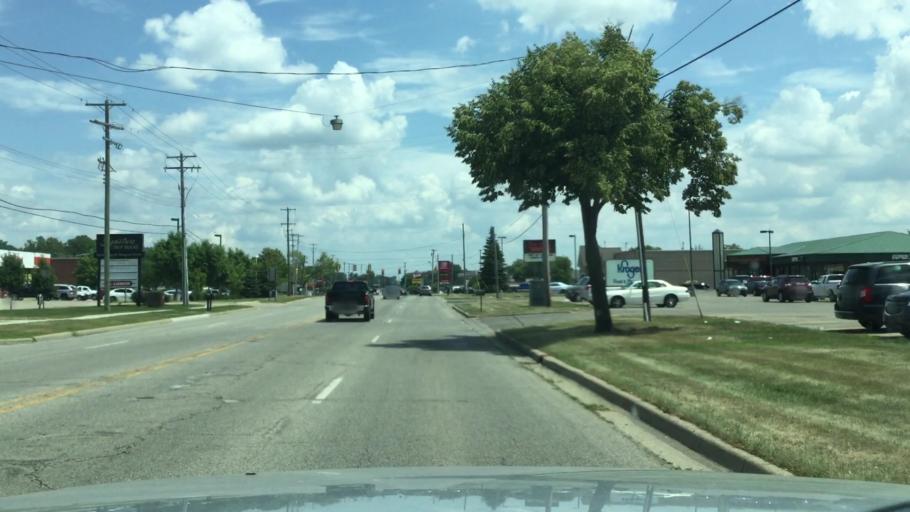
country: US
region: Michigan
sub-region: Genesee County
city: Flushing
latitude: 43.0600
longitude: -83.8161
